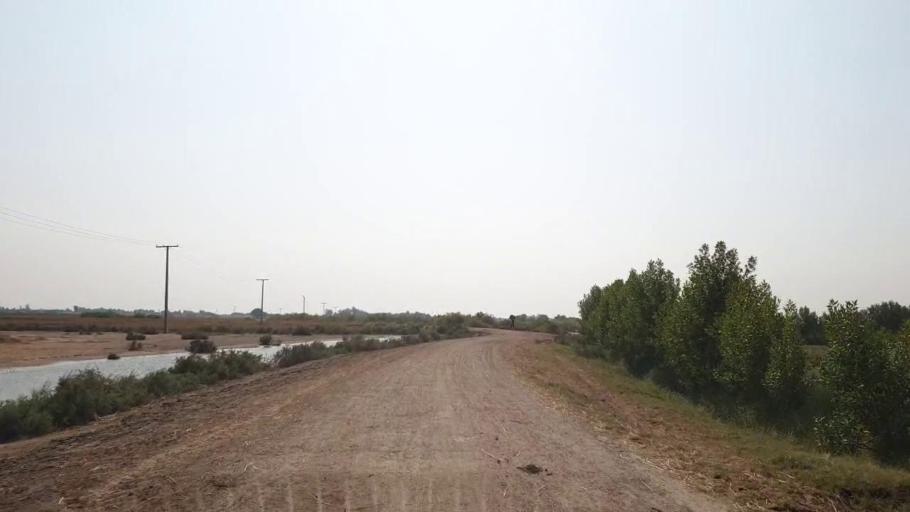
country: PK
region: Sindh
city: Tando Muhammad Khan
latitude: 25.0477
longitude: 68.4519
